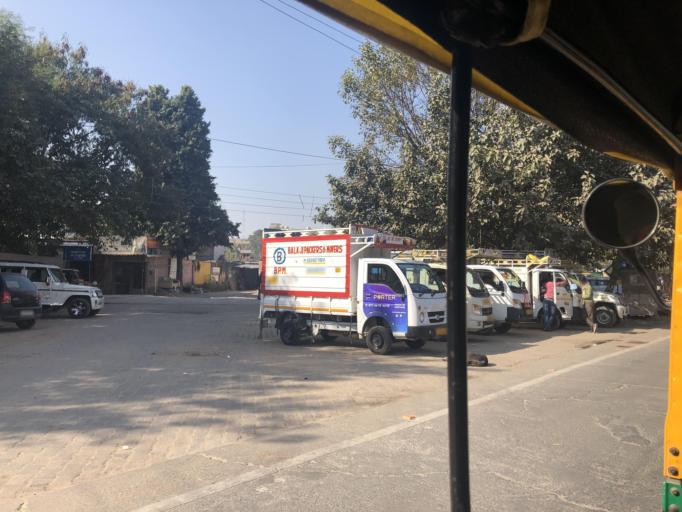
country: IN
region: Haryana
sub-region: Gurgaon
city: Gurgaon
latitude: 28.4475
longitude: 77.0745
